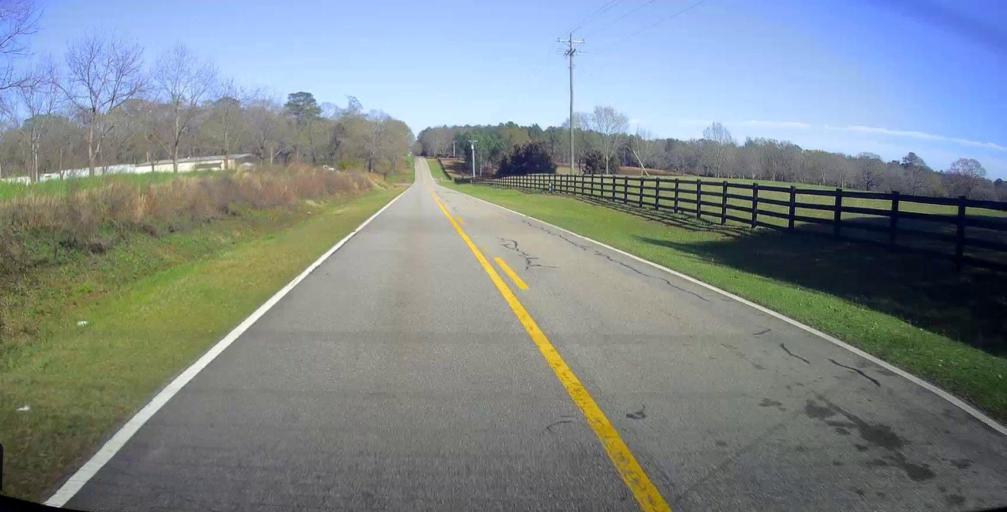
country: US
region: Georgia
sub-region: Peach County
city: Byron
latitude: 32.6442
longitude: -83.8286
